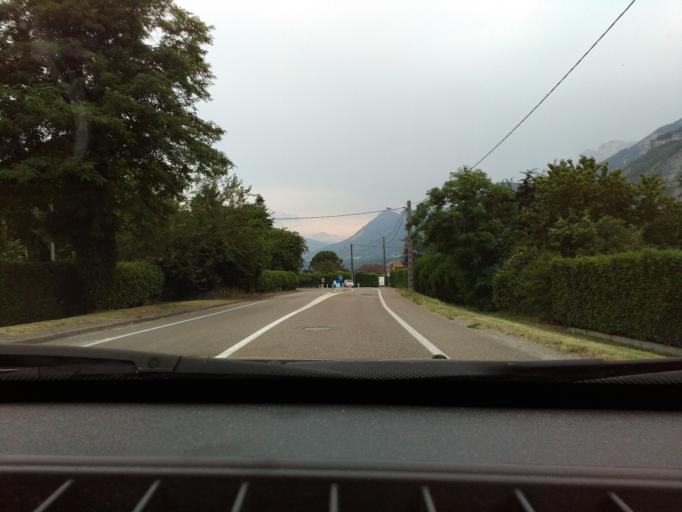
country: FR
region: Rhone-Alpes
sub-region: Departement de l'Isere
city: Vif
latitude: 45.0451
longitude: 5.6653
